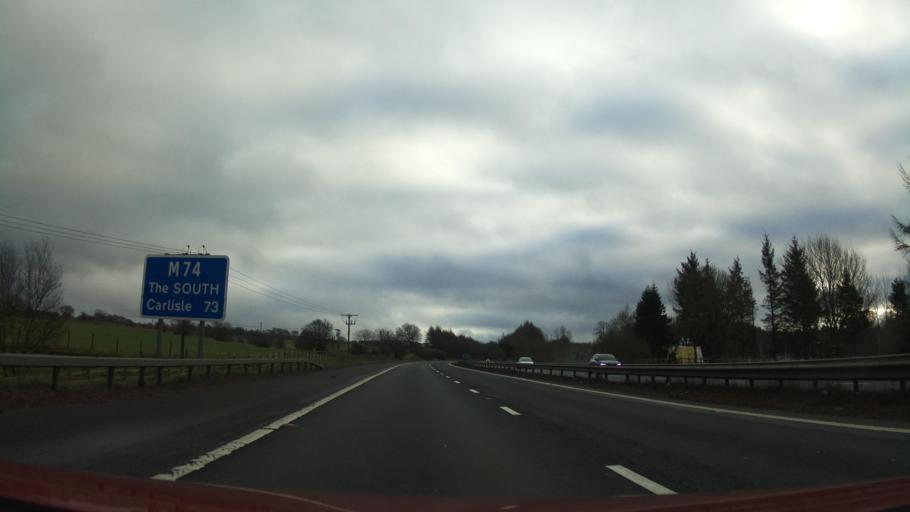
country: GB
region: Scotland
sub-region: South Lanarkshire
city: Lesmahagow
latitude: 55.6443
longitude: -3.8822
